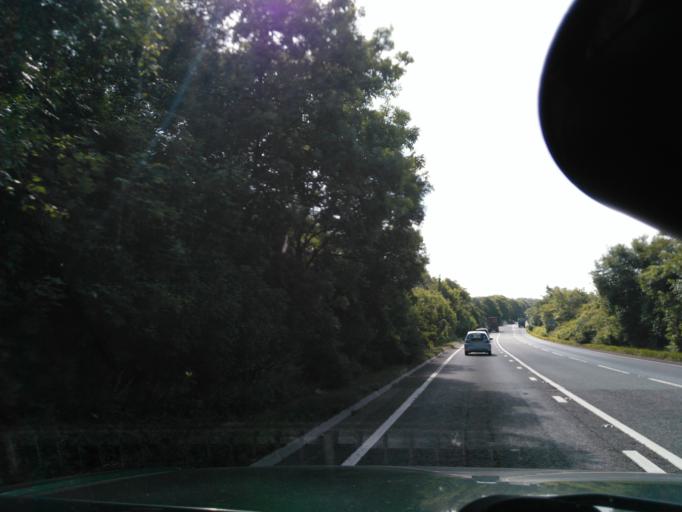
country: GB
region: England
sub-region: Wiltshire
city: Downton
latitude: 51.0205
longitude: -1.6966
